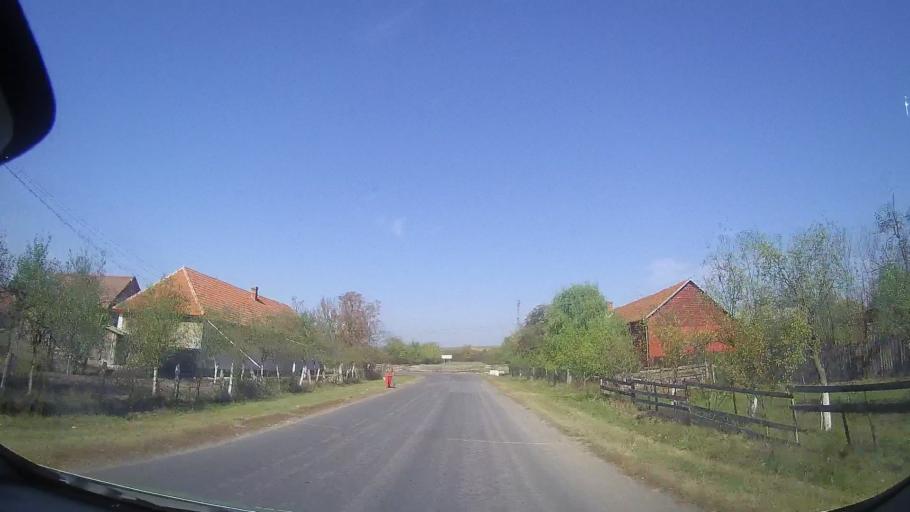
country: RO
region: Timis
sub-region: Comuna Ghizela
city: Ghizela
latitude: 45.8211
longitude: 21.7411
